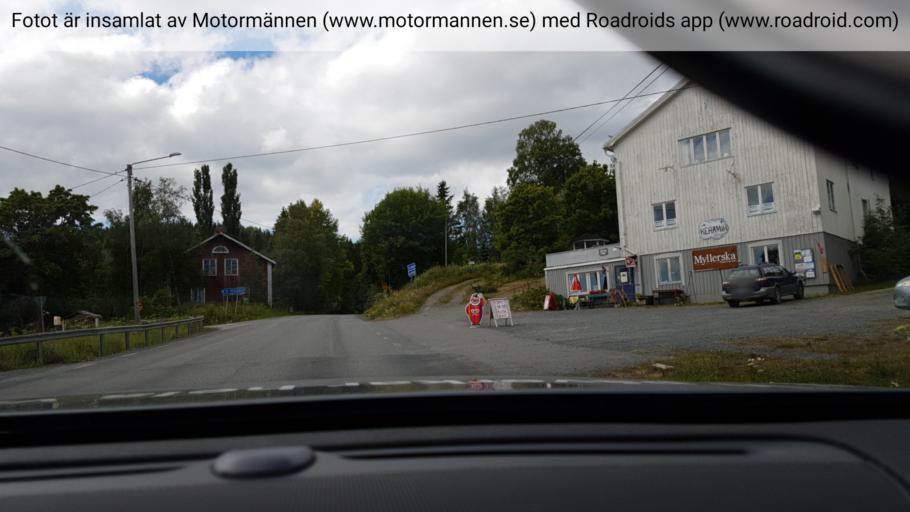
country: SE
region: Vaesternorrland
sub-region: Kramfors Kommun
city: Nordingra
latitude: 62.9358
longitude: 18.2355
